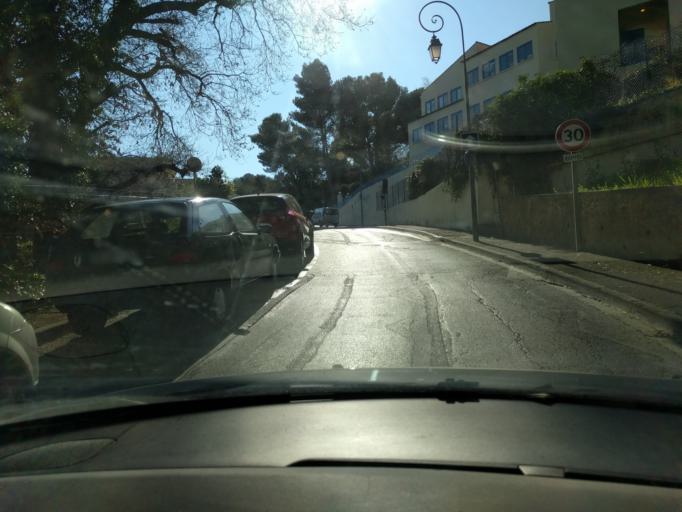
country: FR
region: Provence-Alpes-Cote d'Azur
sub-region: Departement des Alpes-Maritimes
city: Mougins
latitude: 43.6030
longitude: 6.9941
